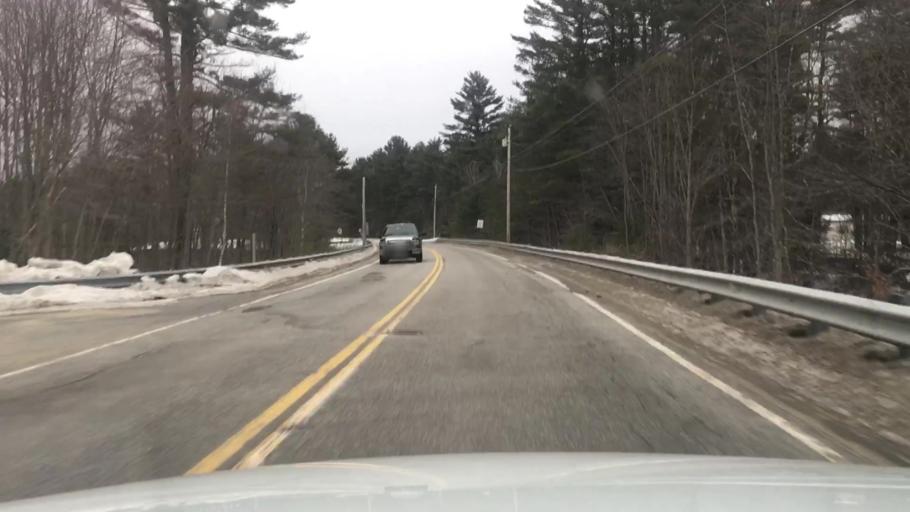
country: US
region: Maine
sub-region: York County
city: Newfield
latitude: 43.6547
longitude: -70.8380
